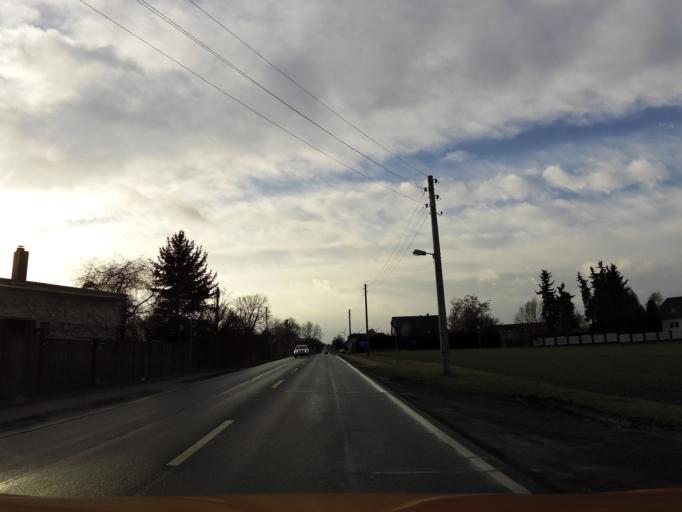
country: DE
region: Saxony-Anhalt
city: Ebendorf
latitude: 52.1871
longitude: 11.5816
